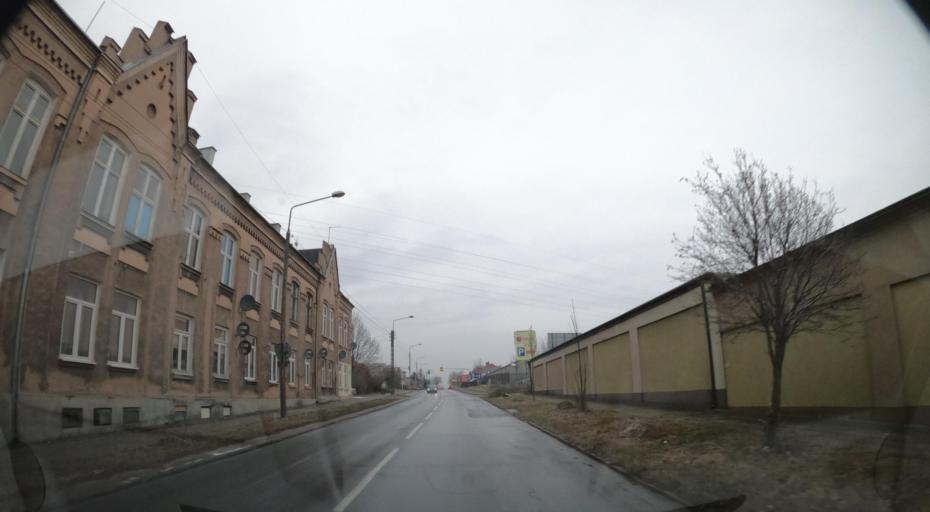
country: PL
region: Masovian Voivodeship
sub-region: Radom
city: Radom
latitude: 51.3848
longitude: 21.1234
